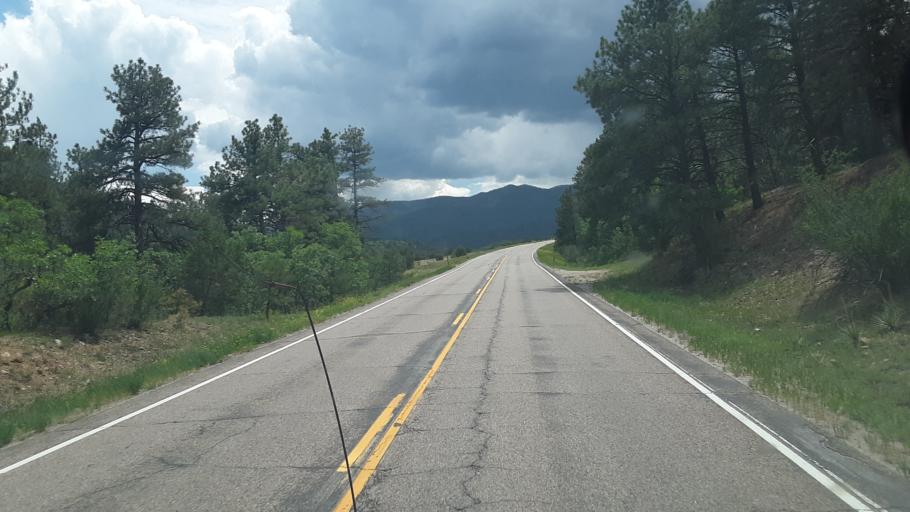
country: US
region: Colorado
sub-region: Fremont County
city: Florence
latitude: 38.2053
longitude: -105.0982
